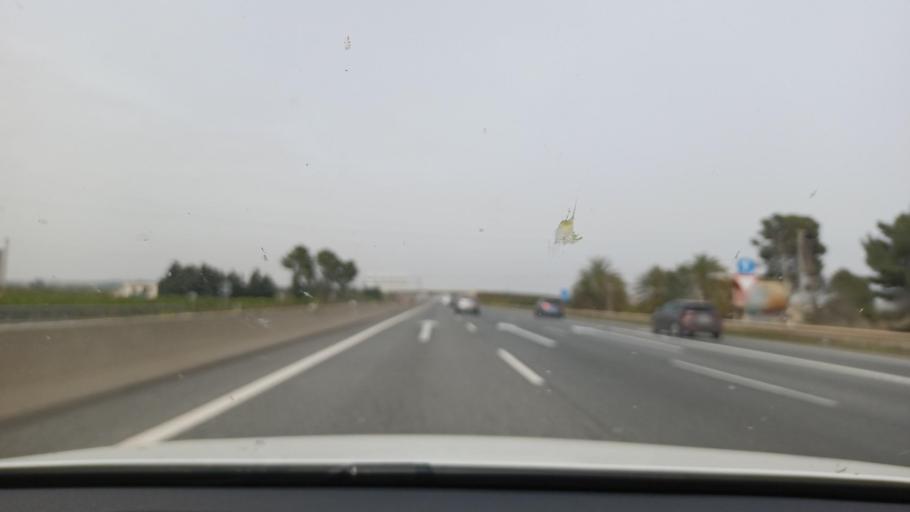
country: ES
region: Valencia
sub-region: Provincia de Valencia
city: Alginet
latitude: 39.2887
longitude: -0.4544
